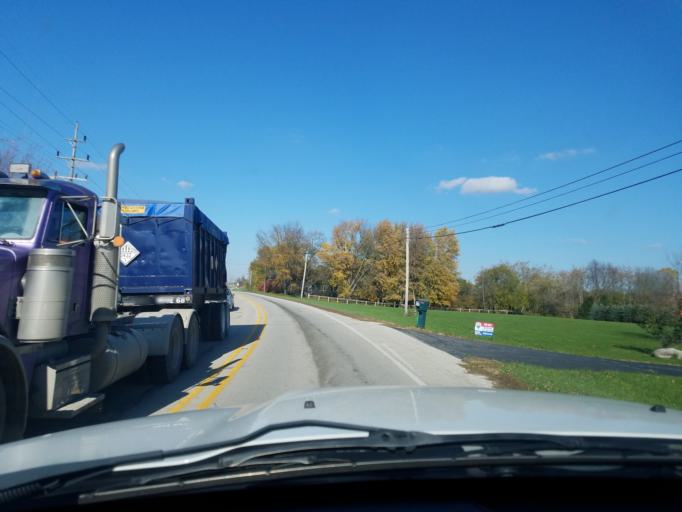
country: US
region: Indiana
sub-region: Hendricks County
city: Pittsboro
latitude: 39.9304
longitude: -86.6196
